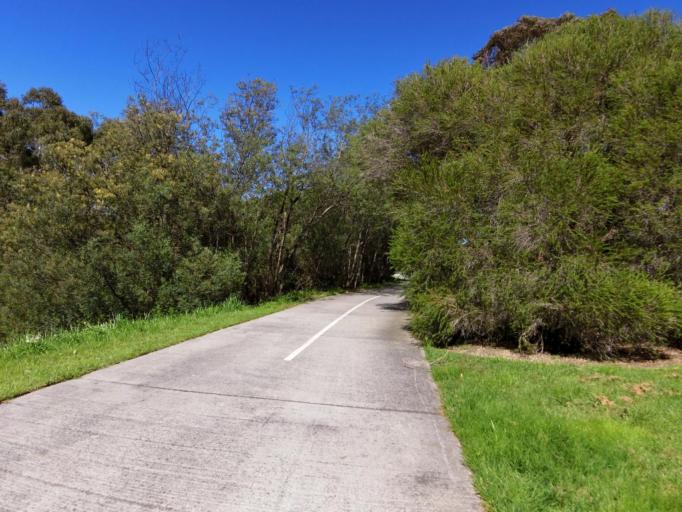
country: AU
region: Victoria
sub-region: Monash
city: Mulgrave
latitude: -37.9272
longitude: 145.2053
